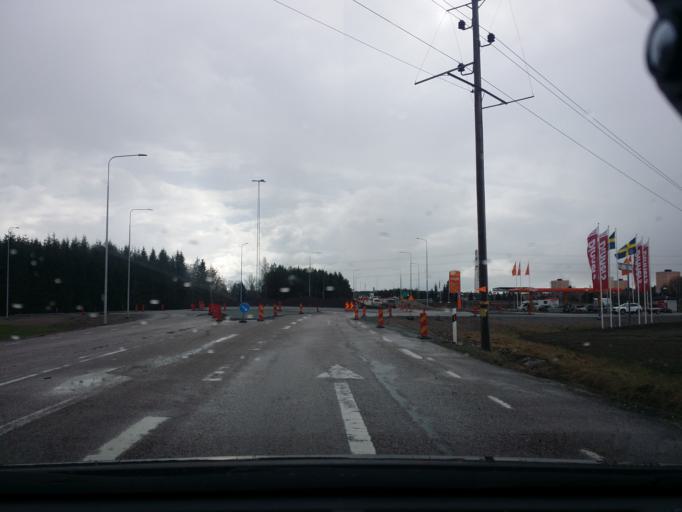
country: SE
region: Uppsala
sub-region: Enkopings Kommun
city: Enkoping
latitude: 59.6592
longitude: 17.0776
